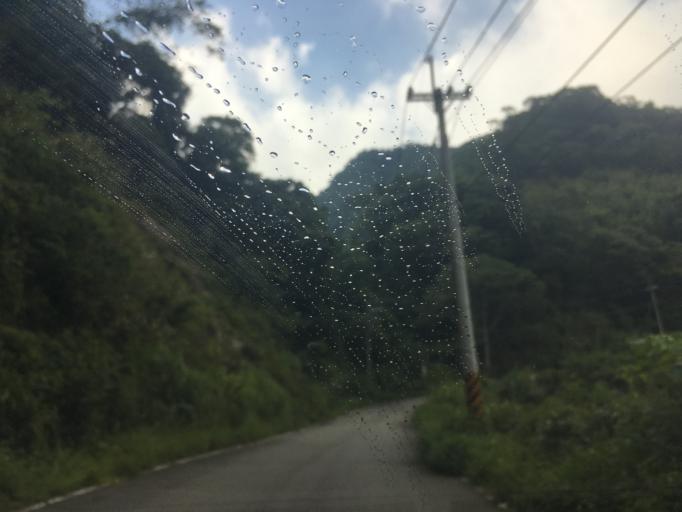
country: TW
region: Taiwan
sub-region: Miaoli
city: Miaoli
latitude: 24.3909
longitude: 120.9729
